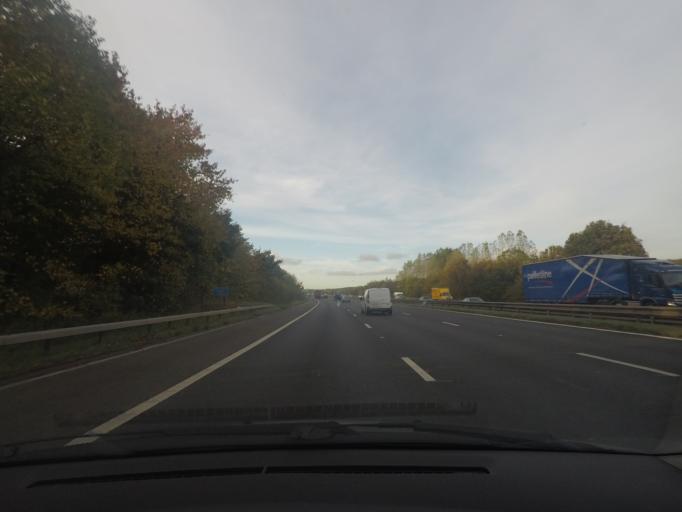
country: GB
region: England
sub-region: Barnsley
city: Darton
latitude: 53.5884
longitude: -1.5365
